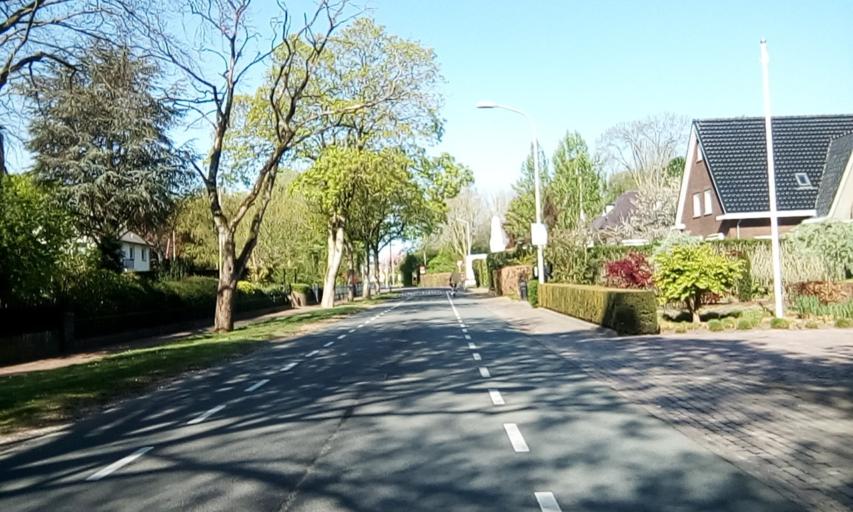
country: NL
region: Gelderland
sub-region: Gemeente Tiel
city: Tiel
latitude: 51.8912
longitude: 5.4189
